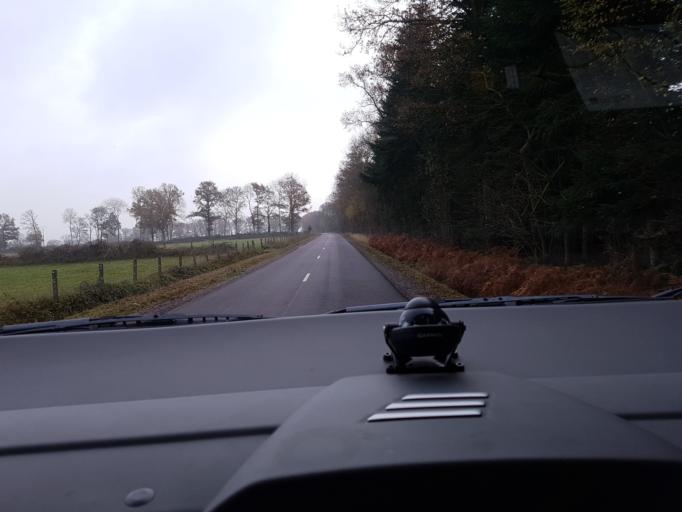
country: FR
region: Lower Normandy
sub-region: Departement de l'Orne
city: Mortree
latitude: 48.6347
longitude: 0.0188
